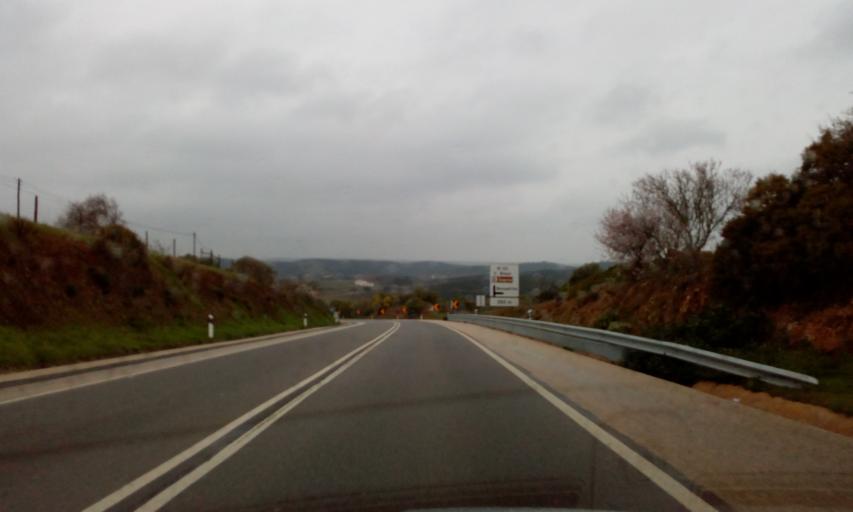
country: PT
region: Faro
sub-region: Vila do Bispo
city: Vila do Bispo
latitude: 37.0931
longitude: -8.8038
